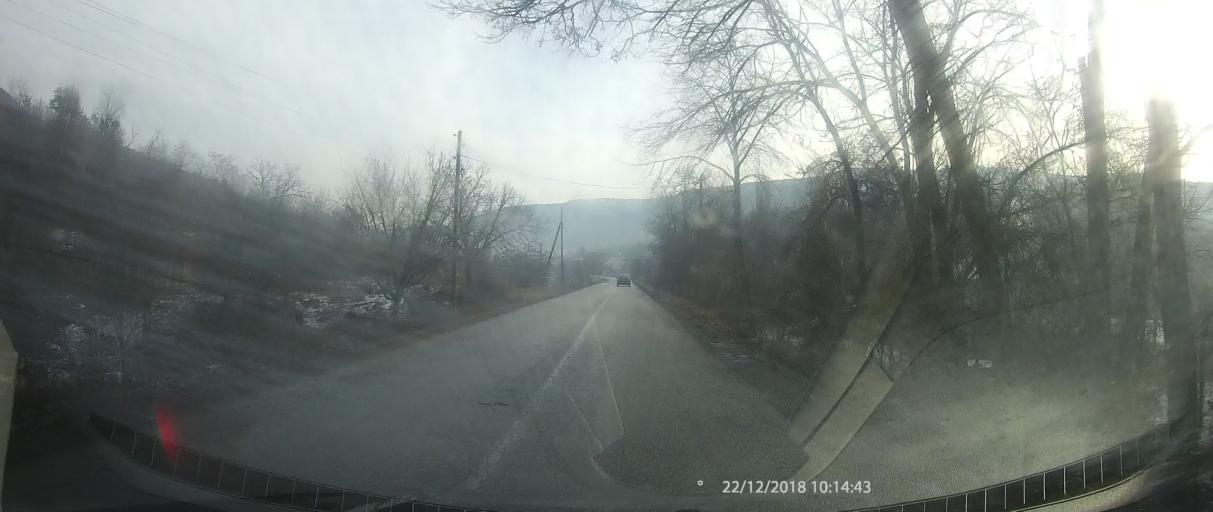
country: MK
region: Kriva Palanka
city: Kriva Palanka
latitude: 42.1766
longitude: 22.2441
